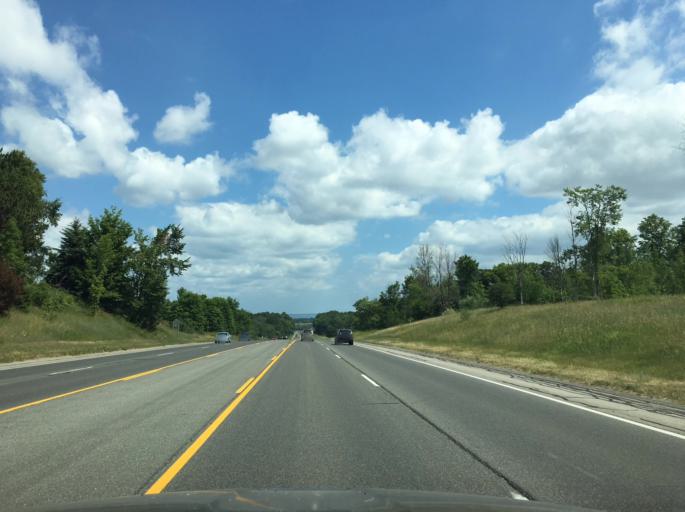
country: US
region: Michigan
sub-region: Grand Traverse County
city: Traverse City
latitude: 44.7039
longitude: -85.6544
